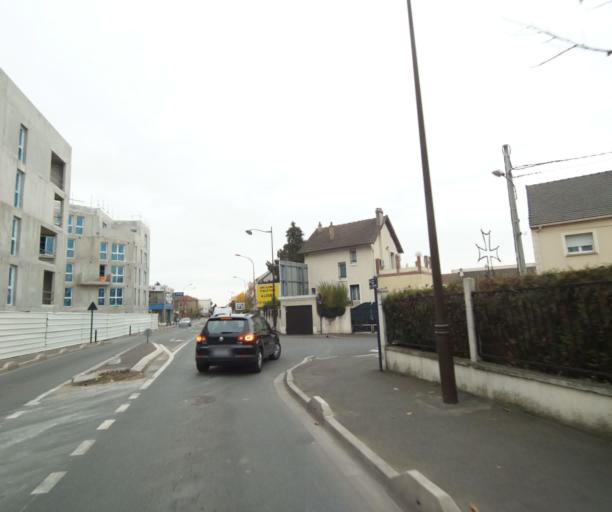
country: FR
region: Ile-de-France
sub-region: Departement du Val-d'Oise
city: Arnouville
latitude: 48.9975
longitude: 2.4185
